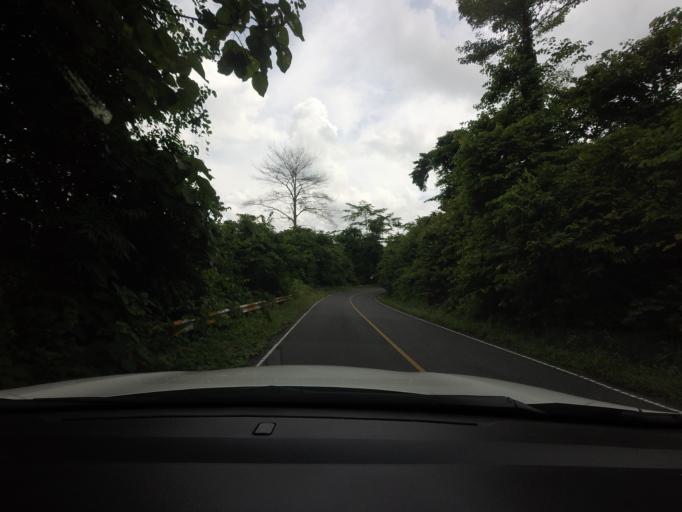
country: TH
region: Nakhon Nayok
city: Pak Phli
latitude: 14.2525
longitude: 101.3819
